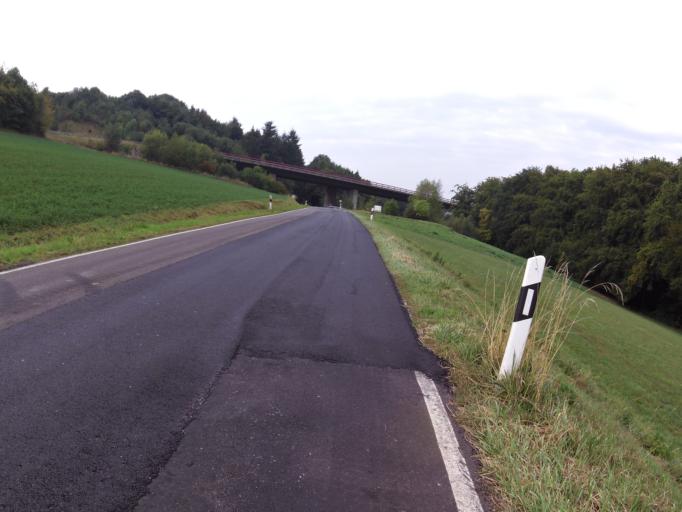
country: DE
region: Rheinland-Pfalz
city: Wilsecker
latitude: 50.0204
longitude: 6.5797
